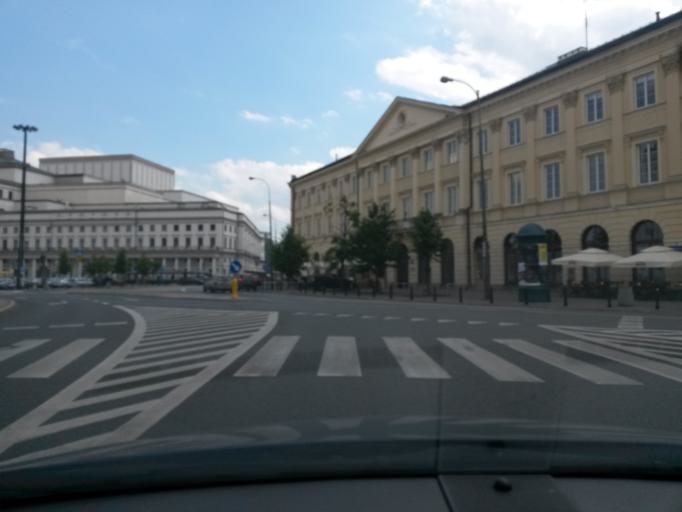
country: PL
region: Masovian Voivodeship
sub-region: Warszawa
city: Warsaw
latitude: 52.2439
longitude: 21.0075
